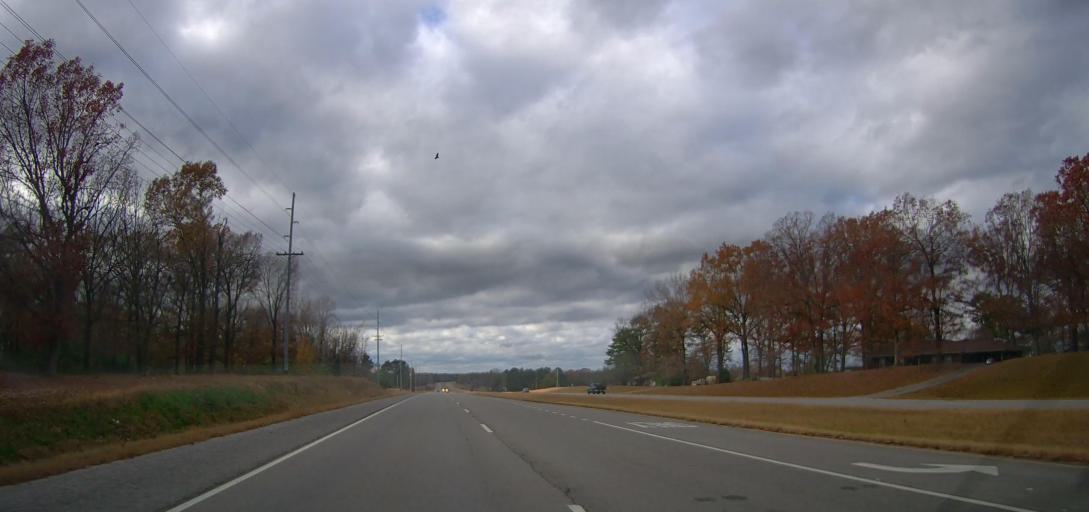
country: US
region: Alabama
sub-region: Lawrence County
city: Town Creek
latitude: 34.5692
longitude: -87.3799
